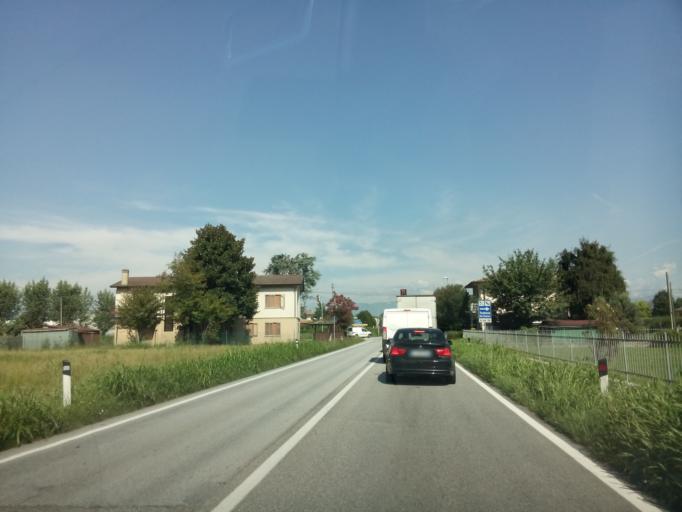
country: IT
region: Veneto
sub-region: Provincia di Padova
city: Grantorto
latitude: 45.5966
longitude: 11.7216
